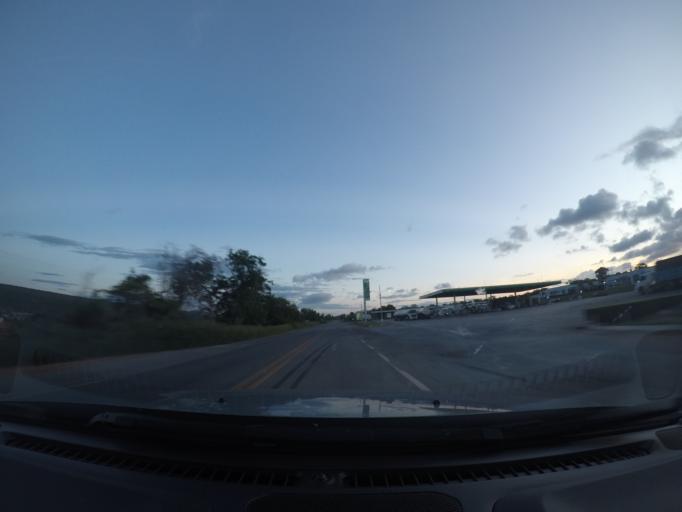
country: BR
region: Bahia
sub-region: Seabra
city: Seabra
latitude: -12.4490
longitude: -41.7512
